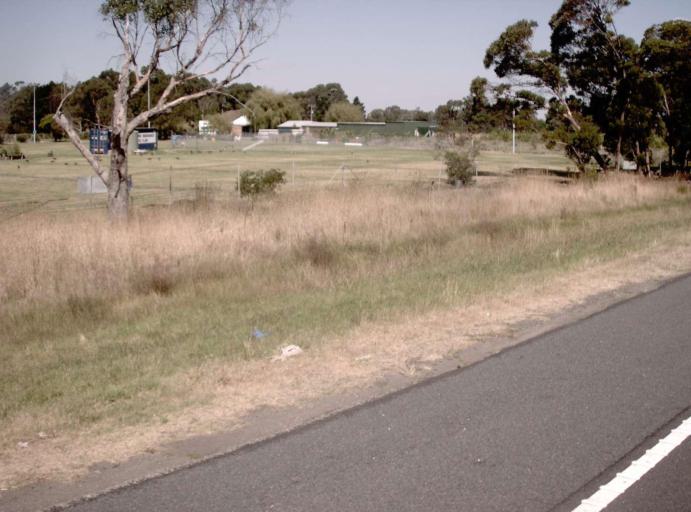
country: AU
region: Victoria
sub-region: Kingston
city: Chelsea Heights
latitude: -38.0275
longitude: 145.1358
